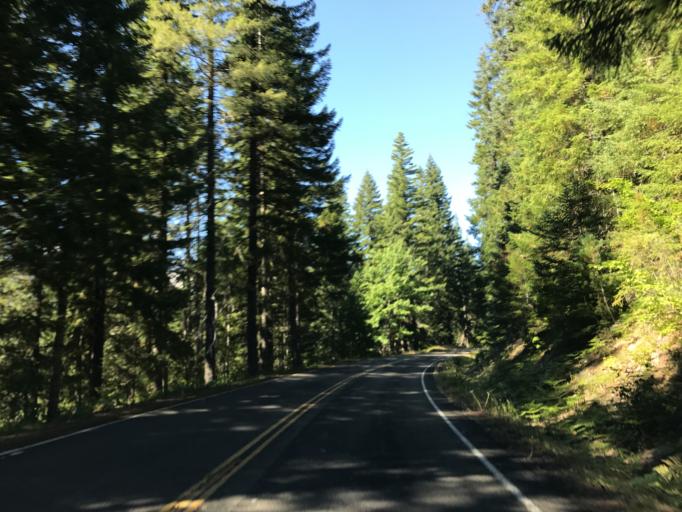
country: US
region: Washington
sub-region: Pierce County
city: Buckley
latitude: 46.7441
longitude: -121.6194
